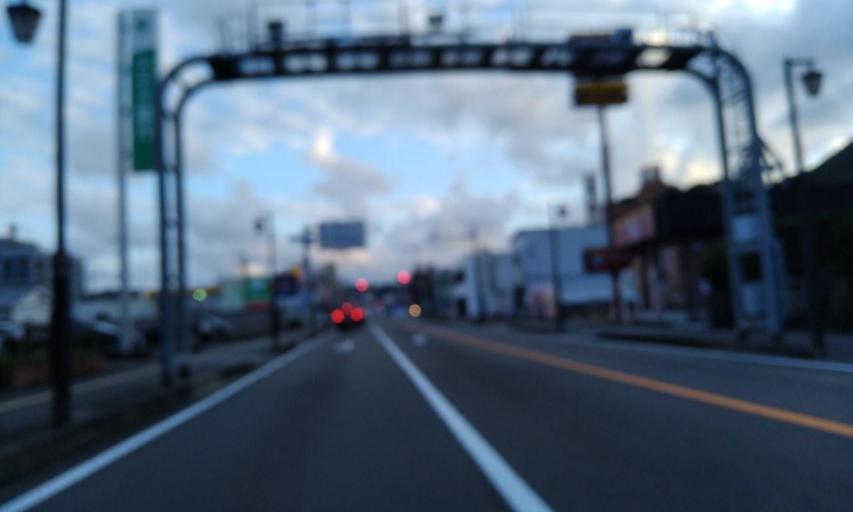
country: JP
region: Wakayama
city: Shingu
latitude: 33.7202
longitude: 135.9868
